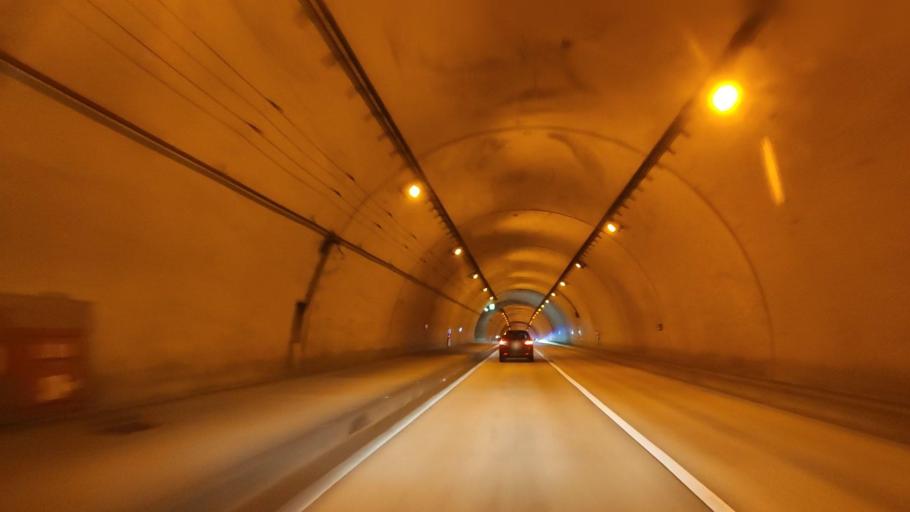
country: JP
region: Ehime
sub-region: Shikoku-chuo Shi
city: Matsuyama
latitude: 33.8811
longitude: 132.7110
